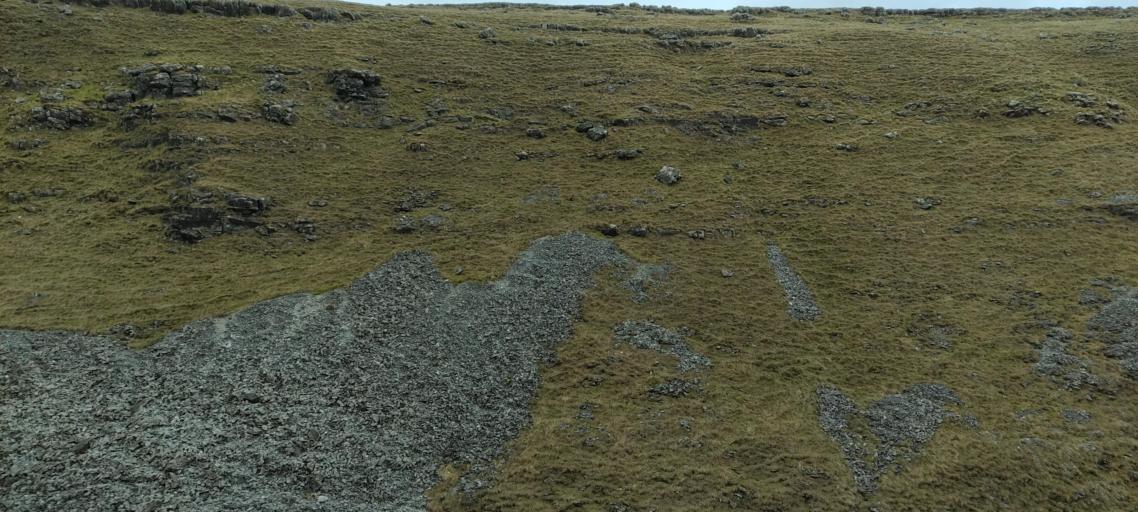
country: GB
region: England
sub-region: North Yorkshire
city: Gargrave
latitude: 54.0735
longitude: -2.1317
